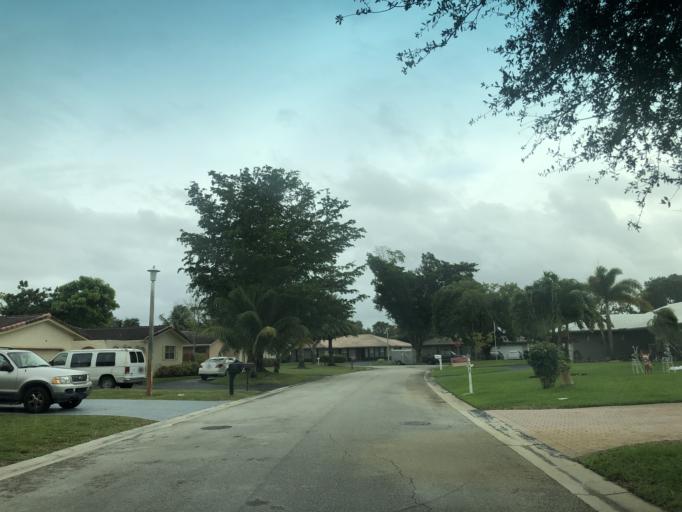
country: US
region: Florida
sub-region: Broward County
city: North Lauderdale
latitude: 26.2406
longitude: -80.2385
